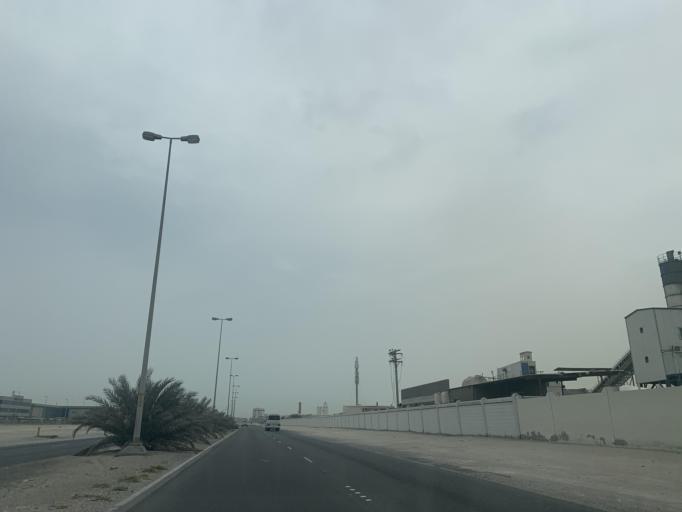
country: BH
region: Muharraq
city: Al Hadd
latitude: 26.2175
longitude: 50.6576
